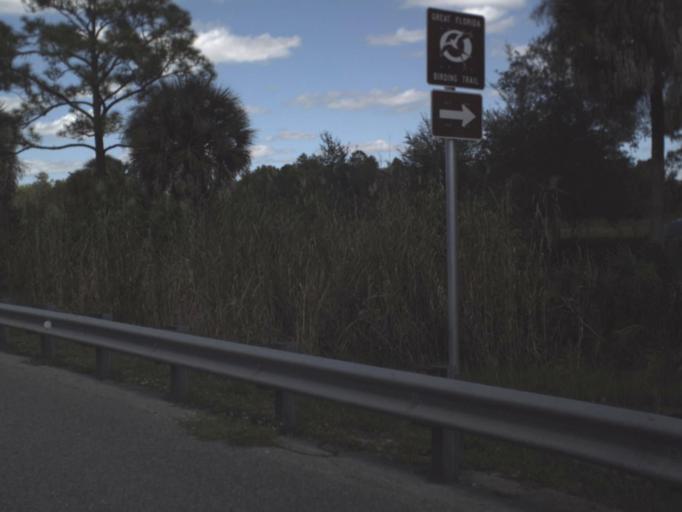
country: US
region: Florida
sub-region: Collier County
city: Lely Resort
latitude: 26.0612
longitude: -81.6957
